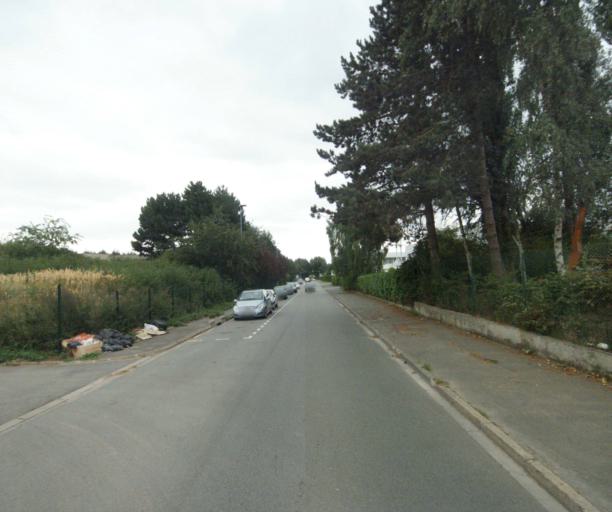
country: FR
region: Nord-Pas-de-Calais
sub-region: Departement du Nord
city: Lesquin
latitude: 50.5818
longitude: 3.1350
